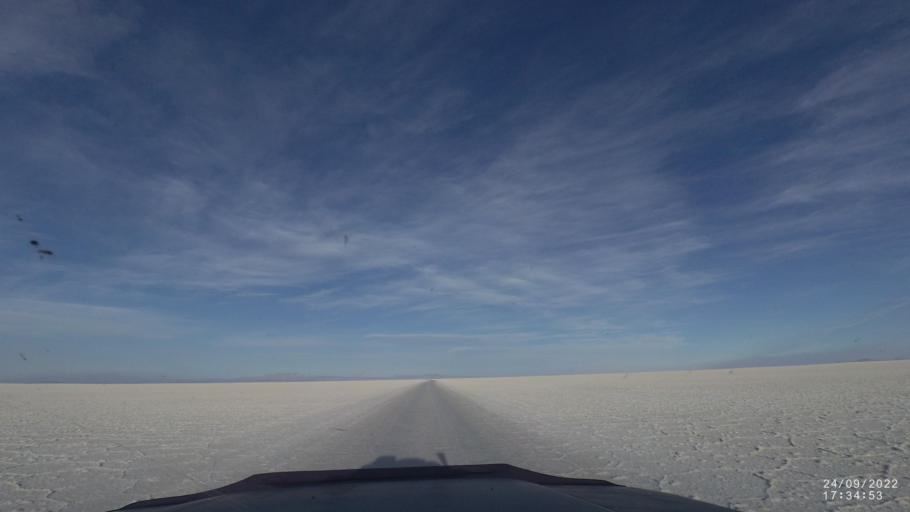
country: BO
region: Potosi
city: Colchani
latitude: -20.3222
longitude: -67.2711
